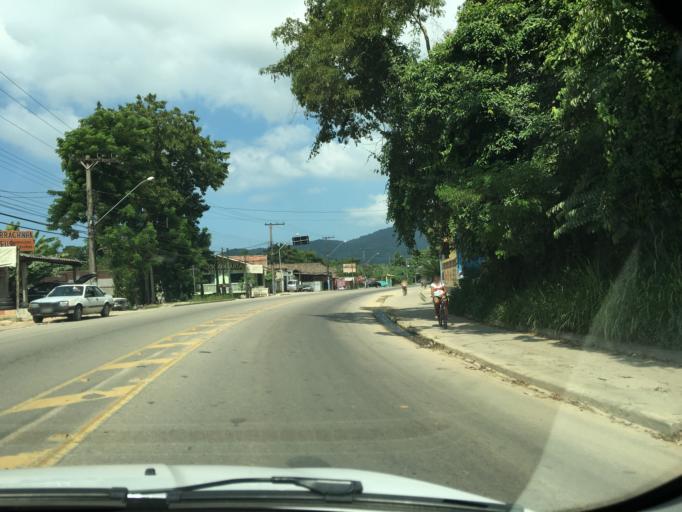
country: BR
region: Sao Paulo
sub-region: Ubatuba
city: Ubatuba
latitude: -23.4313
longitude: -45.1066
